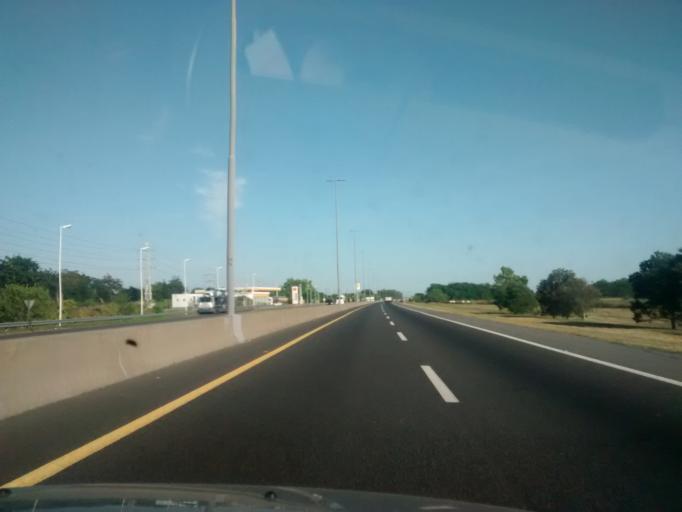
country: AR
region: Buenos Aires
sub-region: Partido de Quilmes
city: Quilmes
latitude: -34.8150
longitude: -58.1109
